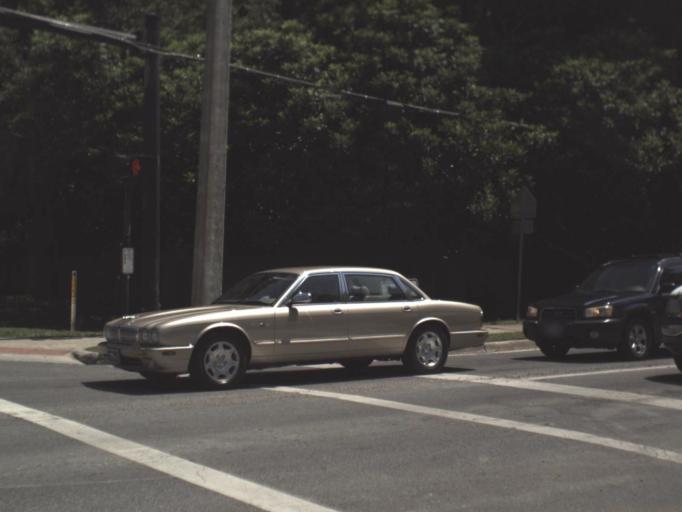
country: US
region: Florida
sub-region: Alachua County
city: Gainesville
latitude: 29.6667
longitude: -82.3723
